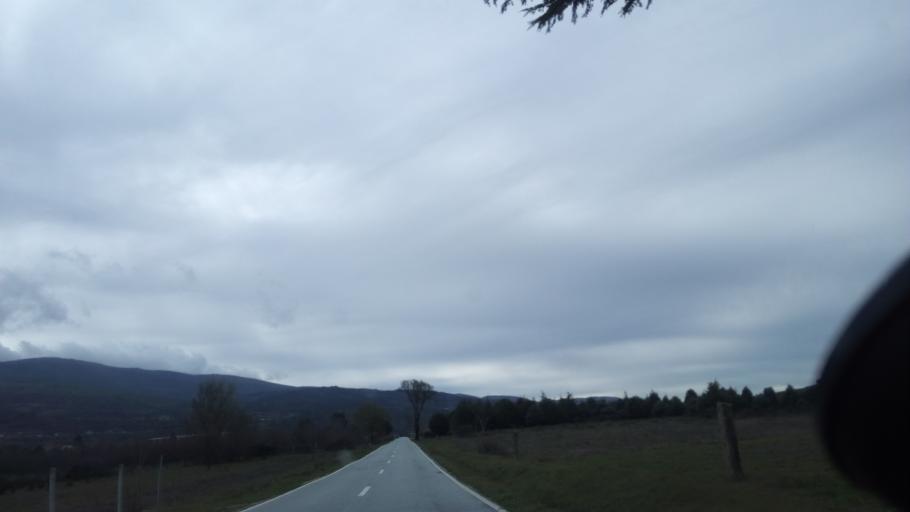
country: PT
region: Guarda
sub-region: Fornos de Algodres
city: Fornos de Algodres
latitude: 40.5423
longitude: -7.5694
